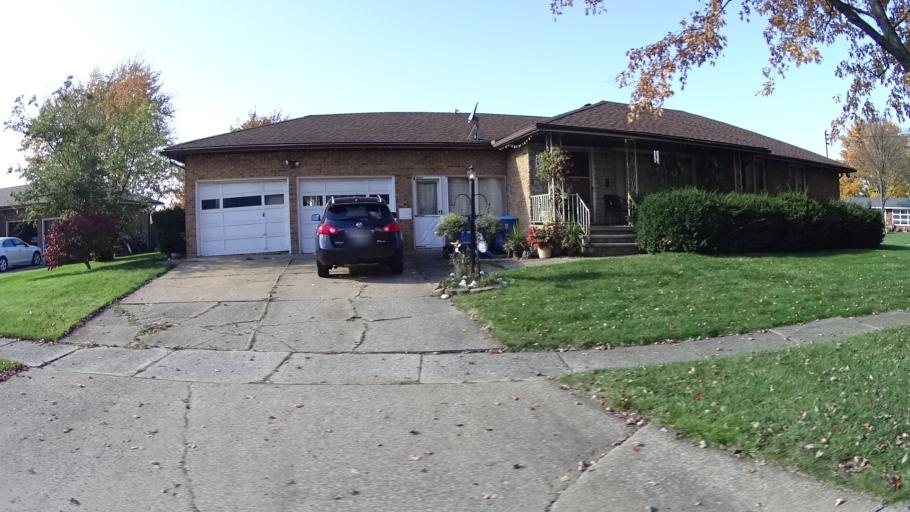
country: US
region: Ohio
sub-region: Lorain County
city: Lorain
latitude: 41.4423
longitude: -82.1893
